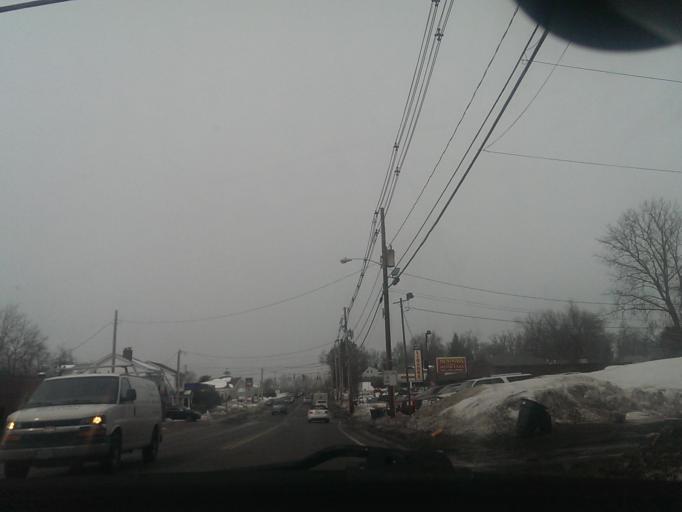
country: US
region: Massachusetts
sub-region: Hampden County
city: East Longmeadow
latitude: 42.0712
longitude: -72.5173
